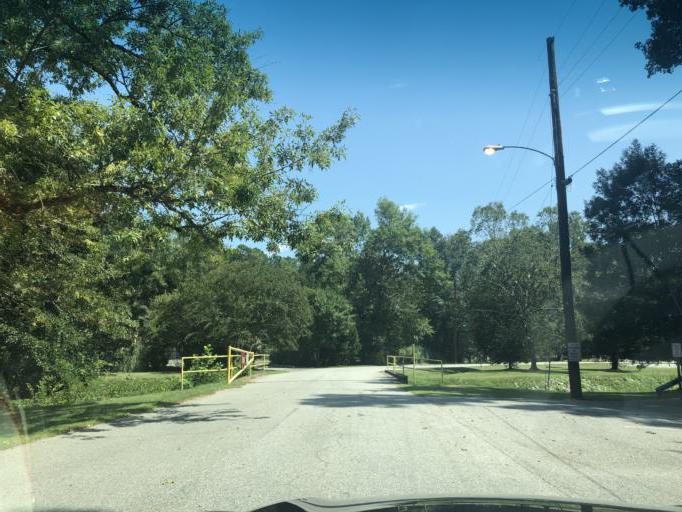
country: US
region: Georgia
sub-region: Muscogee County
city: Columbus
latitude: 32.5140
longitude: -84.9079
